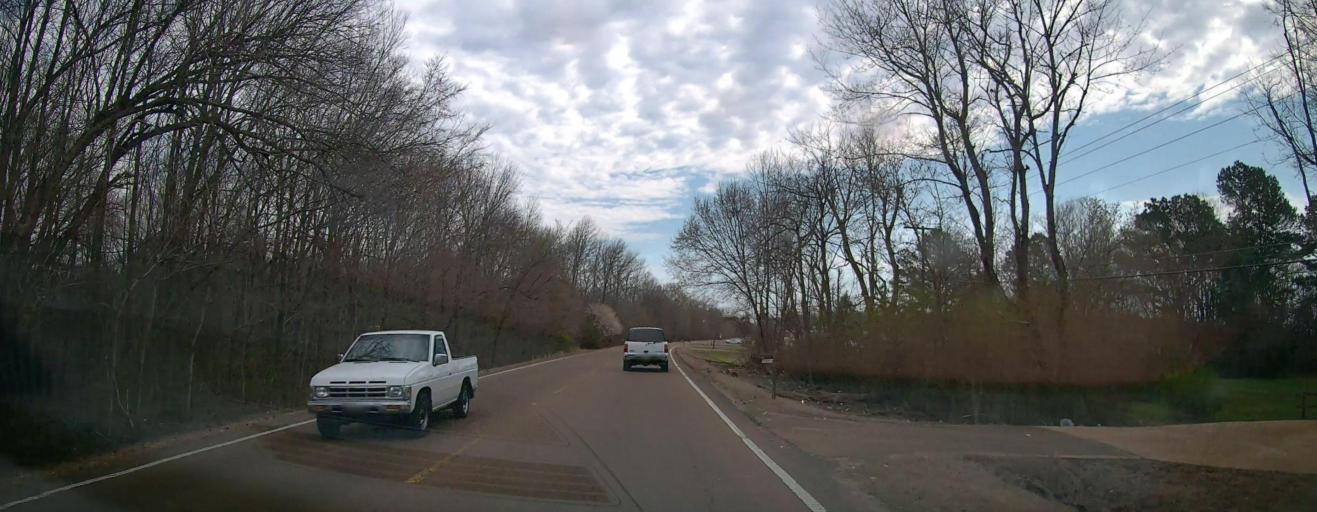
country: US
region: Mississippi
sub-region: Marshall County
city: Byhalia
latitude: 34.8717
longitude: -89.6831
